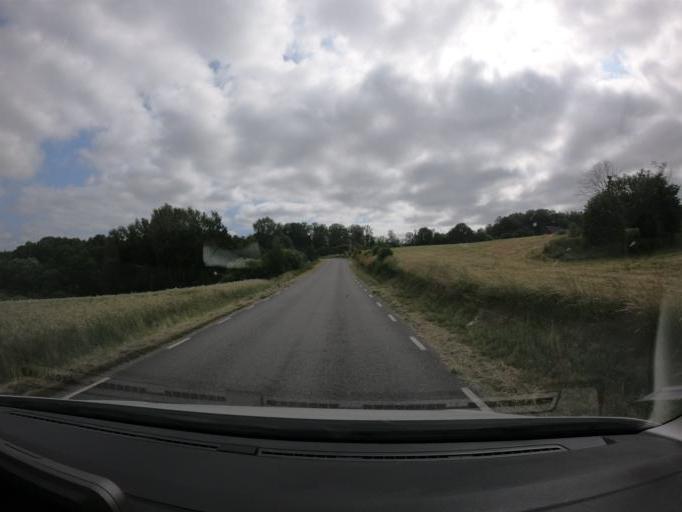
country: SE
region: Skane
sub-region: Hassleholms Kommun
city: Tormestorp
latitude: 56.1442
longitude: 13.6284
